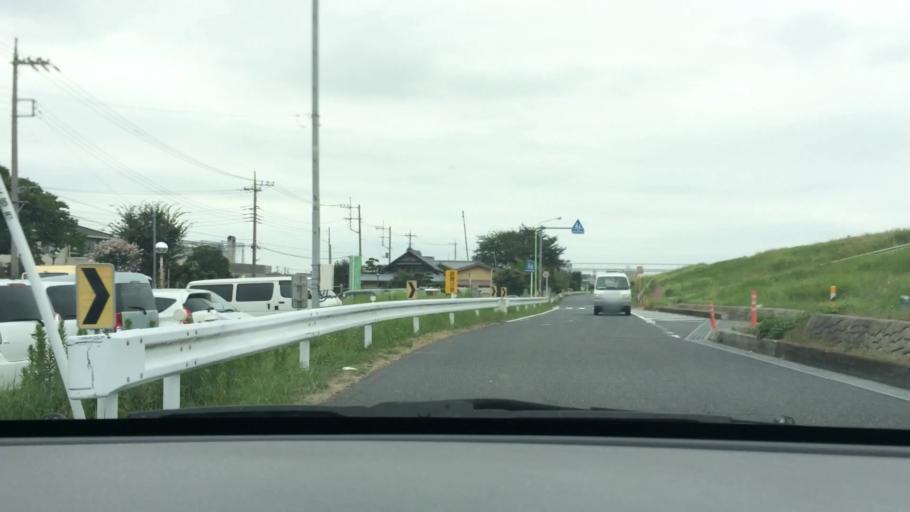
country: JP
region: Chiba
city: Nagareyama
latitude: 35.8335
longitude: 139.8861
